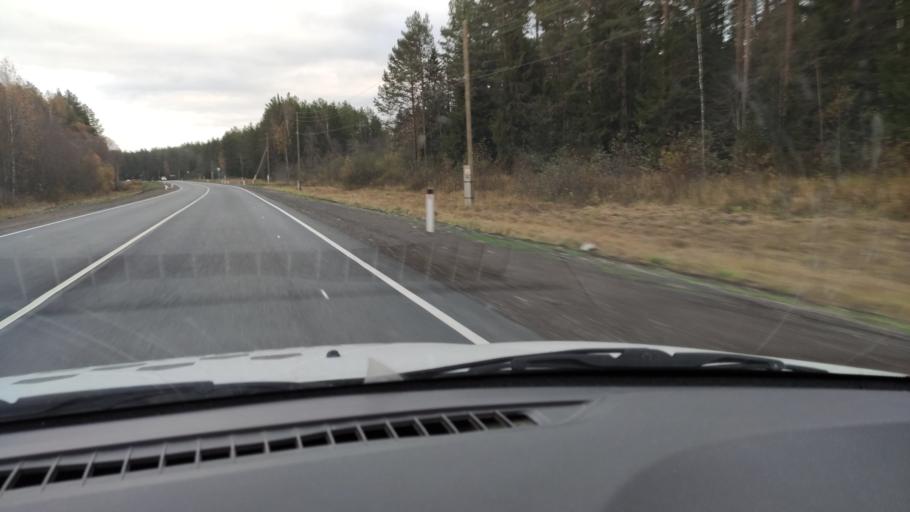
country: RU
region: Kirov
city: Belaya Kholunitsa
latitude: 58.8426
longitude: 50.7720
